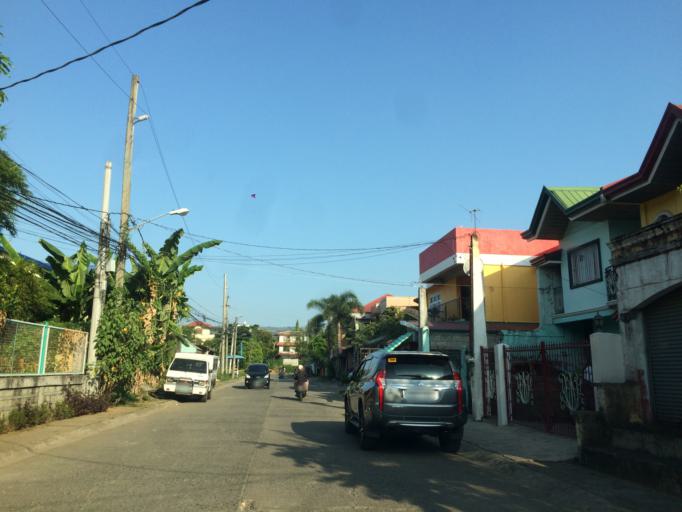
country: PH
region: Calabarzon
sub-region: Province of Rizal
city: San Mateo
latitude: 14.6756
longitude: 121.1222
